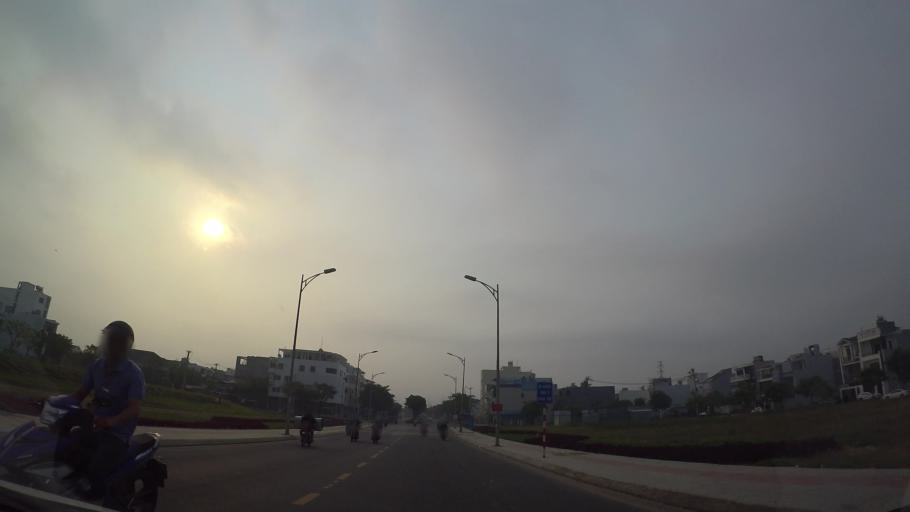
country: VN
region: Da Nang
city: Cam Le
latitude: 16.0232
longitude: 108.2242
